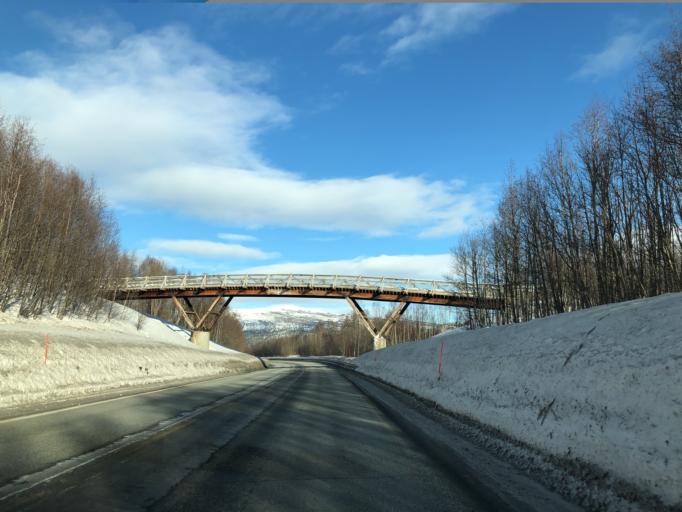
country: NO
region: Troms
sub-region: Malselv
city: Moen
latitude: 69.0779
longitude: 18.5602
